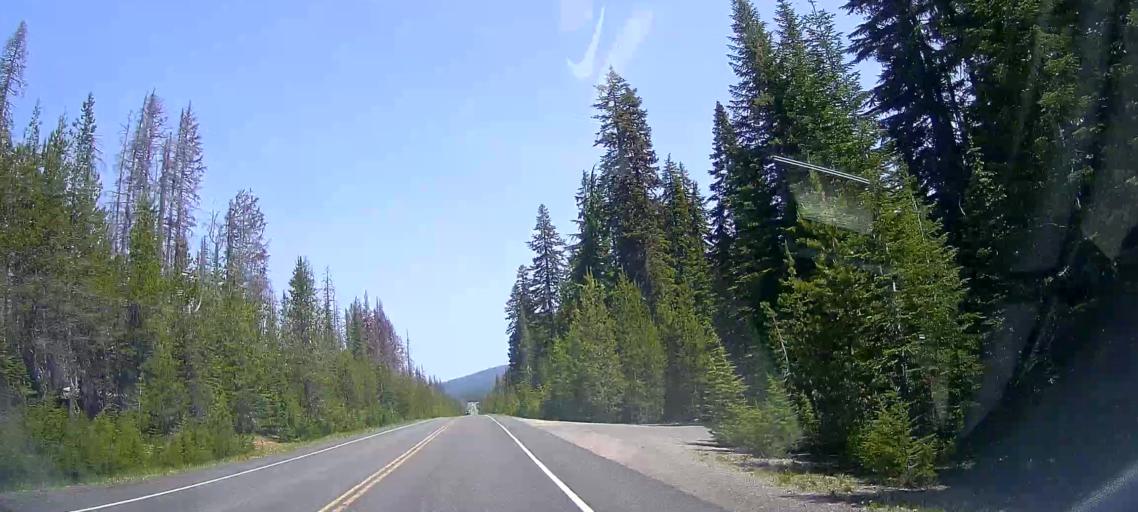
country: US
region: Oregon
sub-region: Lane County
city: Oakridge
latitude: 43.0679
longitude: -122.1196
